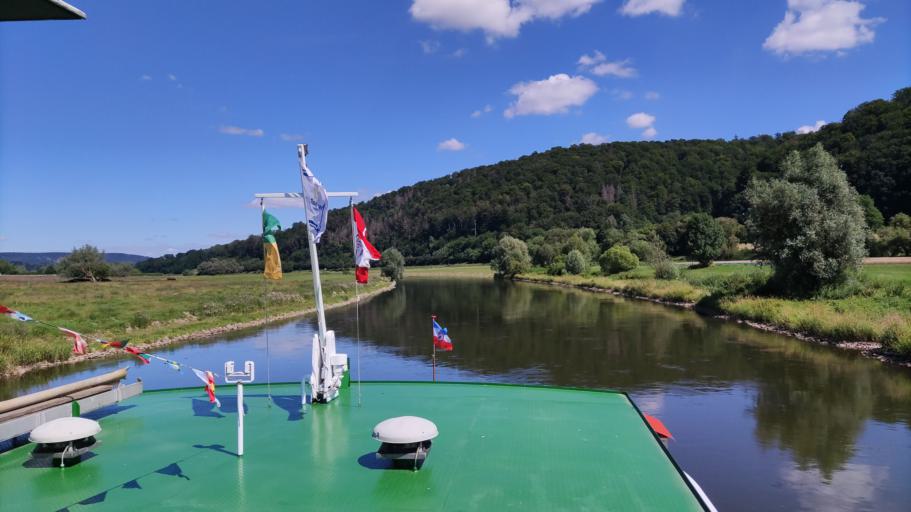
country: DE
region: Lower Saxony
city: Derental
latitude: 51.7000
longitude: 9.4014
